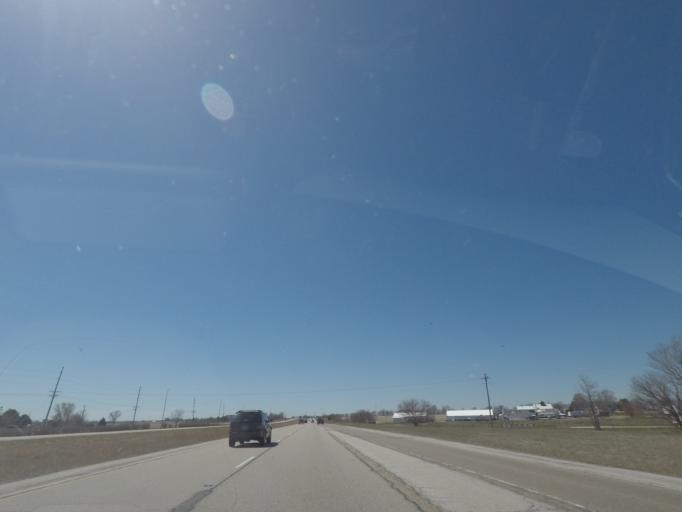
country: US
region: Illinois
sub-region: Logan County
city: Atlanta
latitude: 40.3092
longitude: -89.1673
